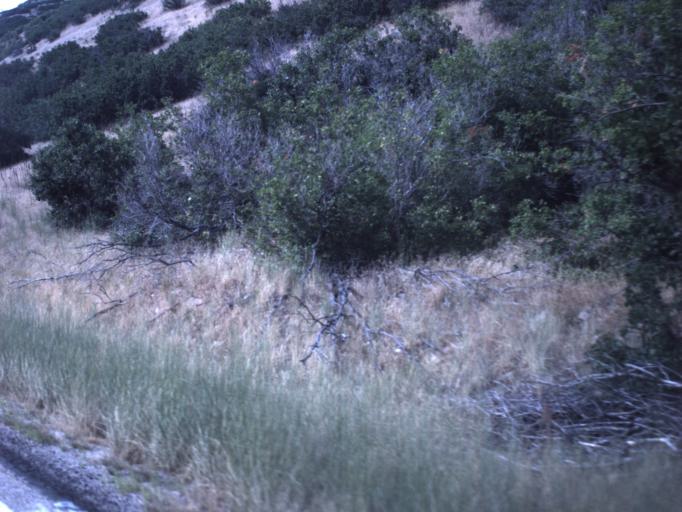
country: US
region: Utah
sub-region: Wasatch County
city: Heber
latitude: 40.4169
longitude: -111.3332
